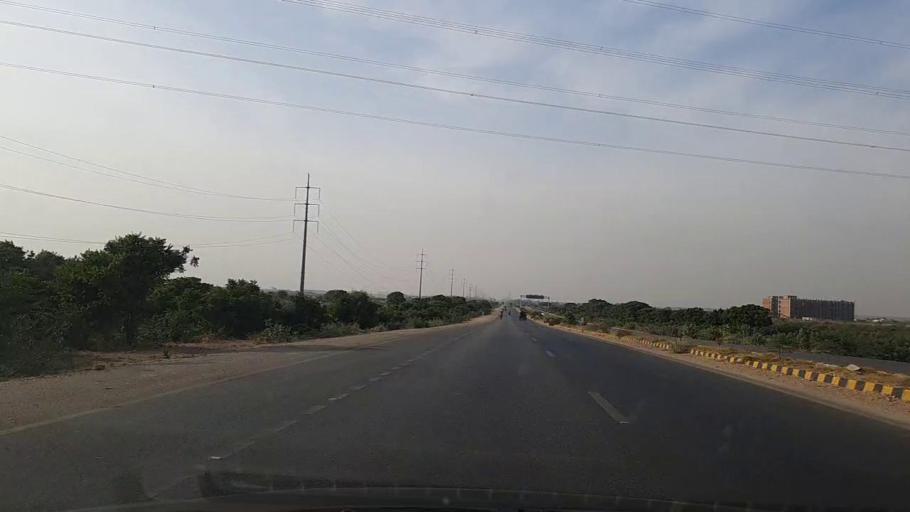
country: PK
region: Sindh
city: Gharo
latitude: 24.7686
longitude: 67.5493
